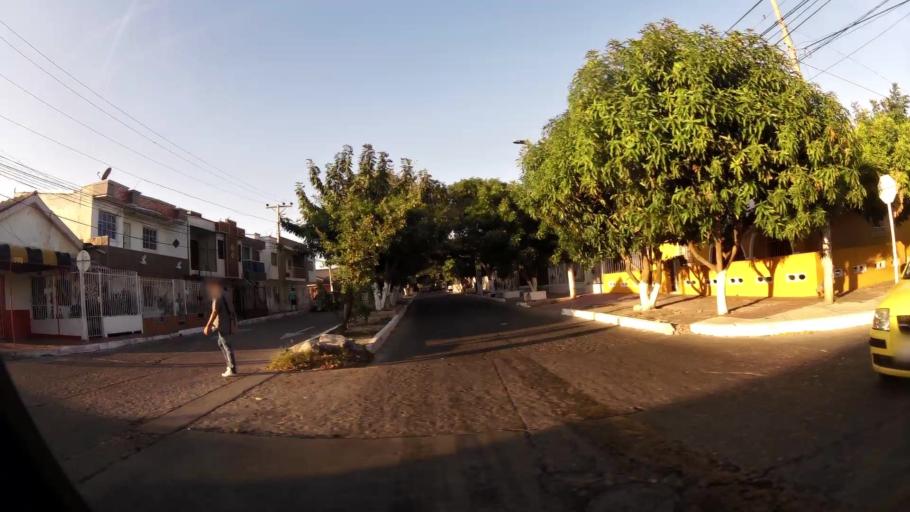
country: CO
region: Atlantico
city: Barranquilla
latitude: 10.9700
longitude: -74.8058
